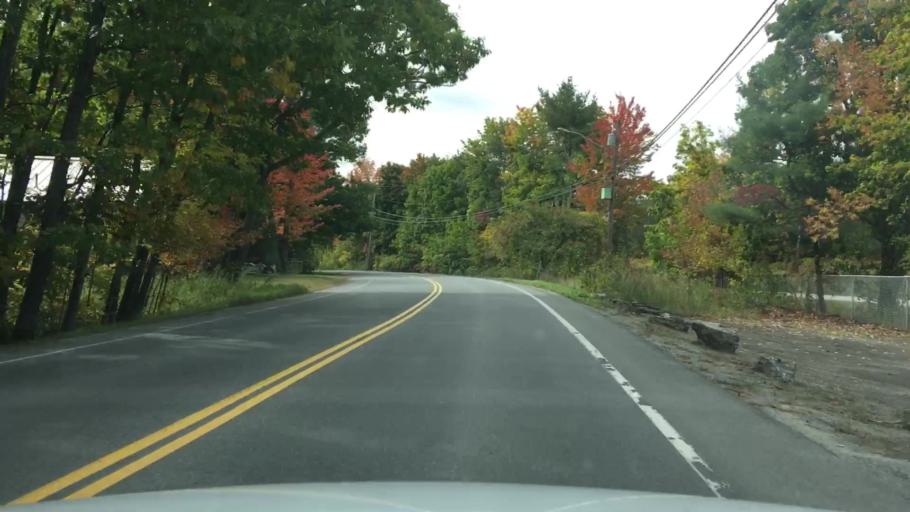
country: US
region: Maine
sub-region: Kennebec County
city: Waterville
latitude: 44.5515
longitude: -69.6763
